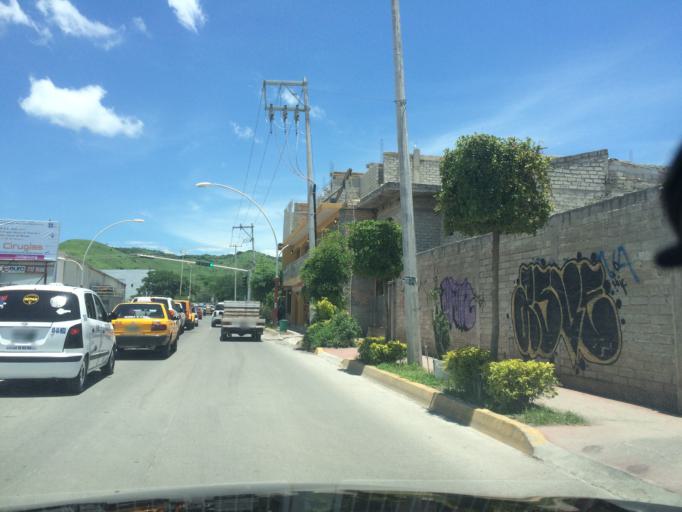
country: MX
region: Nayarit
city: Tepic
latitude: 21.4894
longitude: -104.8641
